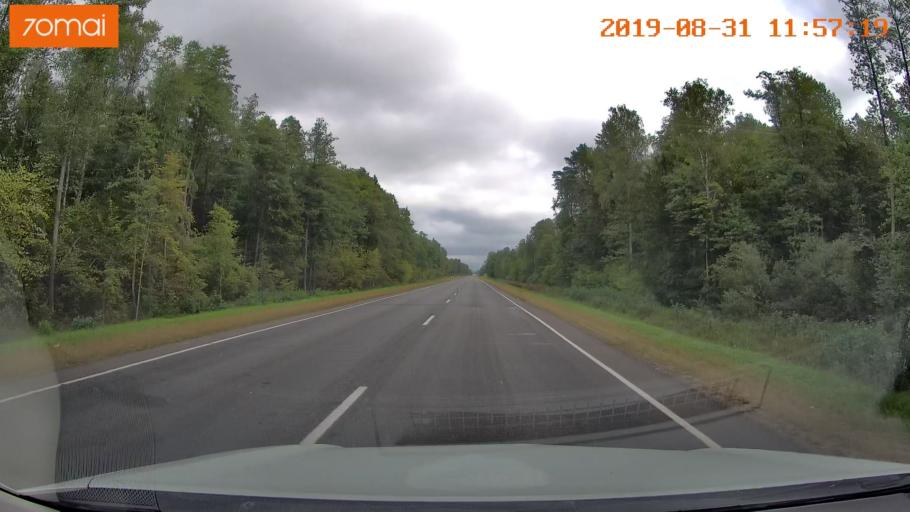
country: BY
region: Mogilev
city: Horad Krychaw
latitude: 53.6553
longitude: 31.6159
